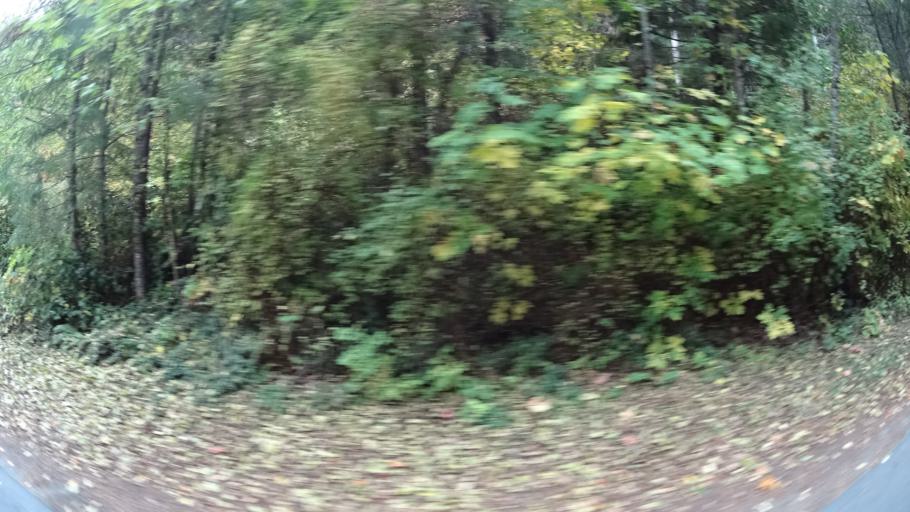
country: US
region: California
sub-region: Siskiyou County
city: Happy Camp
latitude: 41.7898
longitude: -123.3759
